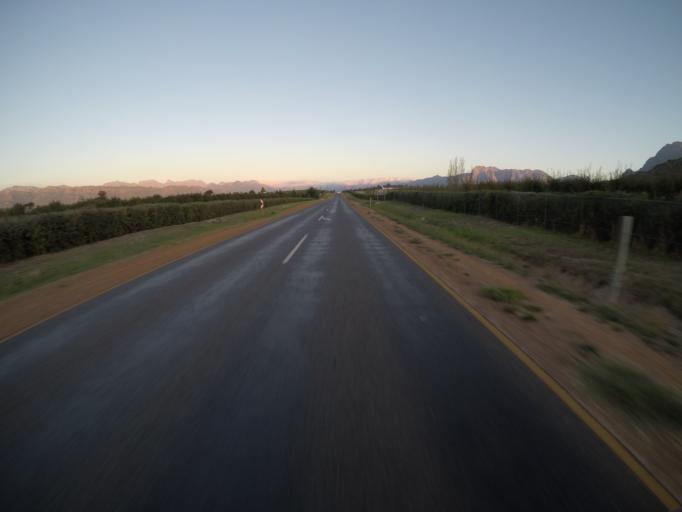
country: ZA
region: Western Cape
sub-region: Cape Winelands District Municipality
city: Paarl
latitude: -33.8236
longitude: 18.9324
